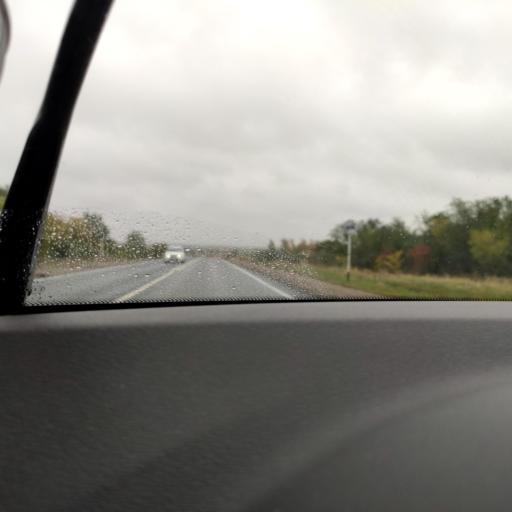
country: RU
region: Samara
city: Mirnyy
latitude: 53.6388
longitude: 50.2311
